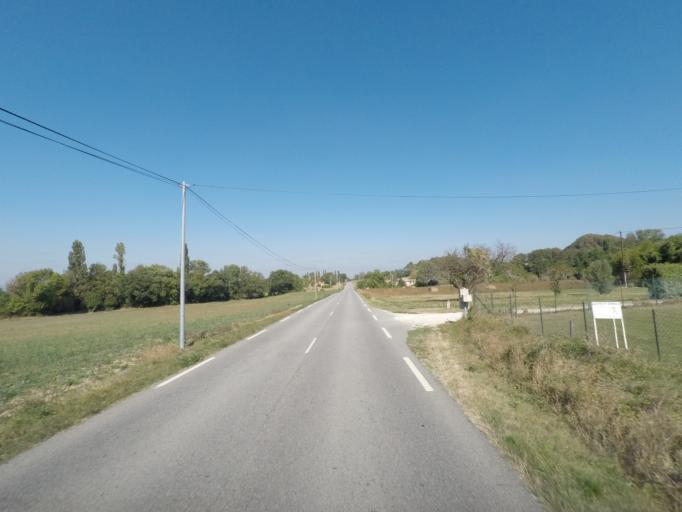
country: FR
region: Rhone-Alpes
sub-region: Departement de la Drome
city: Montmeyran
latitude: 44.8272
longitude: 5.0097
